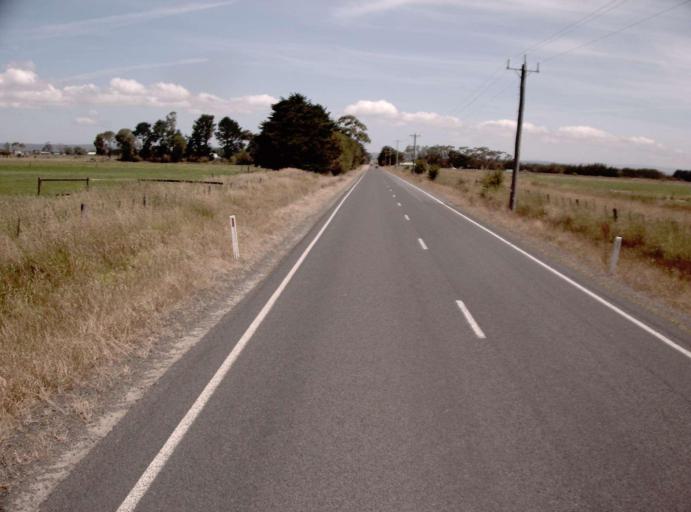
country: AU
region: Victoria
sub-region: Wellington
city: Heyfield
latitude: -38.0809
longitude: 146.8685
